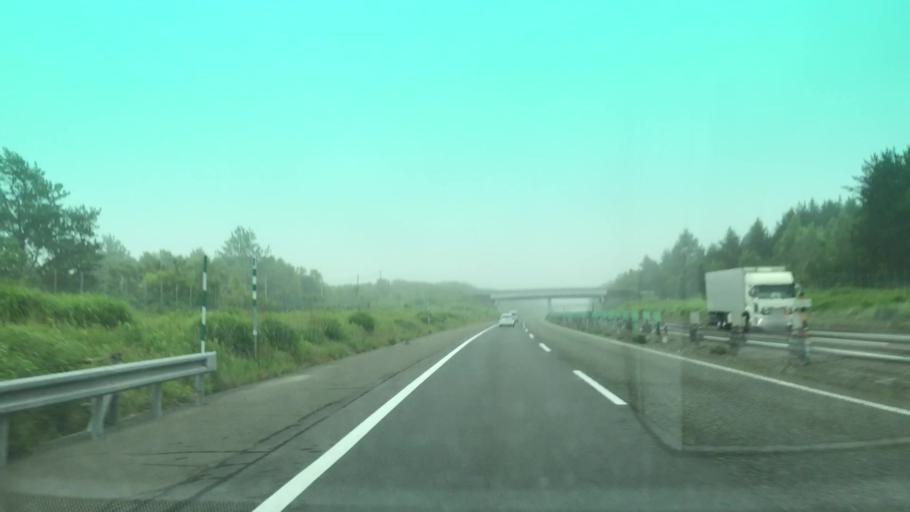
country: JP
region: Hokkaido
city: Chitose
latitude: 42.8285
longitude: 141.6135
